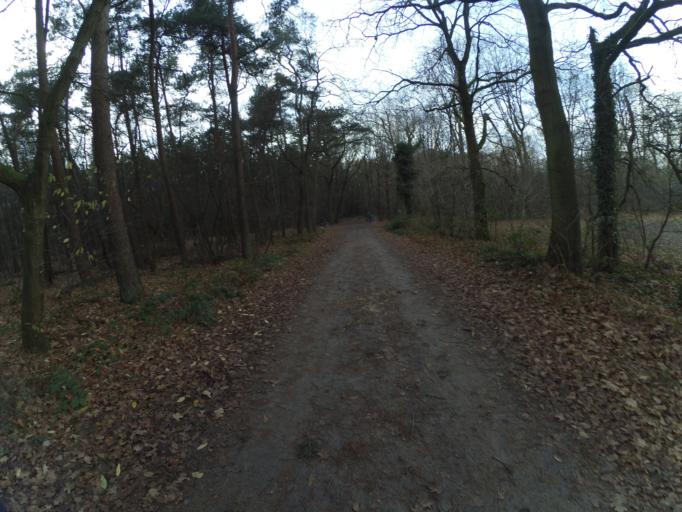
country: NL
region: North Brabant
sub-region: Gemeente Rucphen
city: Rucphen
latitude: 51.5230
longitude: 4.5483
